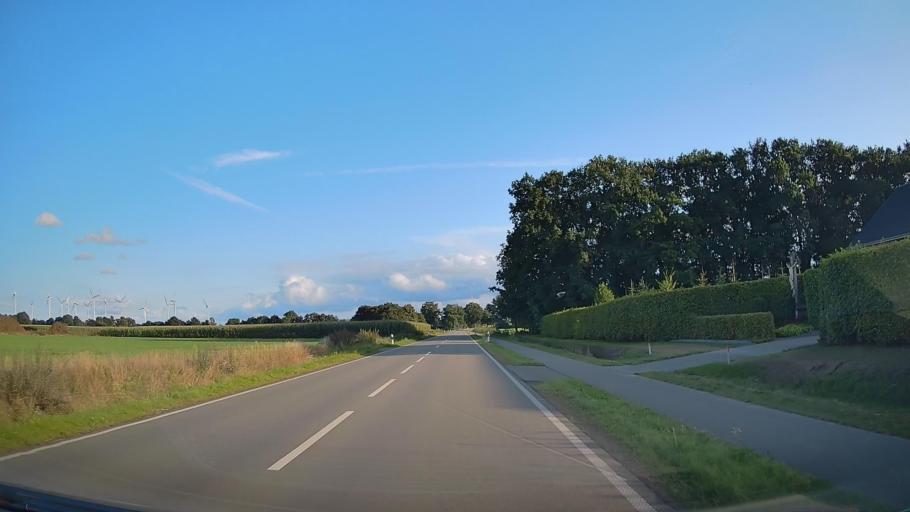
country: DE
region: Lower Saxony
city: Hilkenbrook
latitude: 53.0709
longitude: 7.7190
